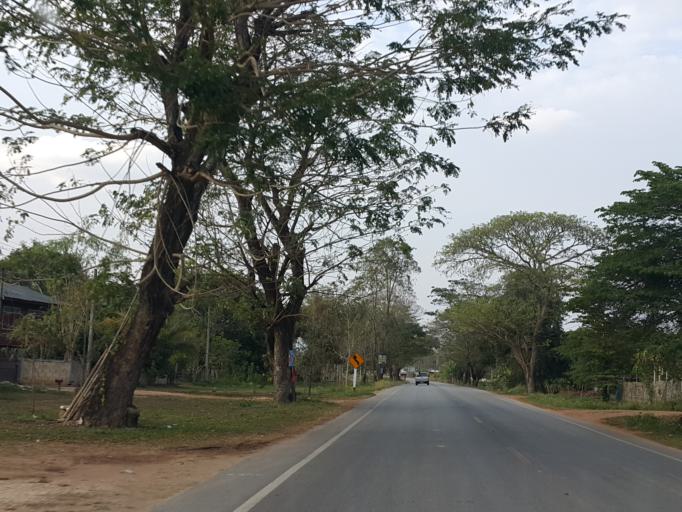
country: TH
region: Lampang
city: Lampang
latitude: 18.4940
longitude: 99.4720
